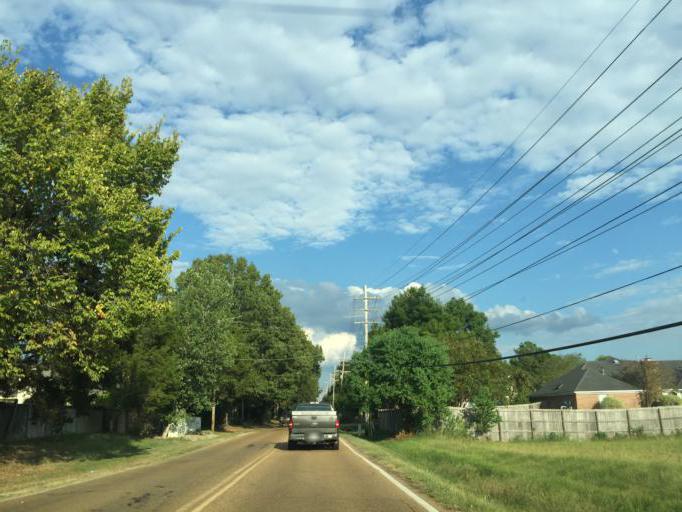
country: US
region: Mississippi
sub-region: Madison County
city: Madison
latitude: 32.4651
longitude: -90.0897
